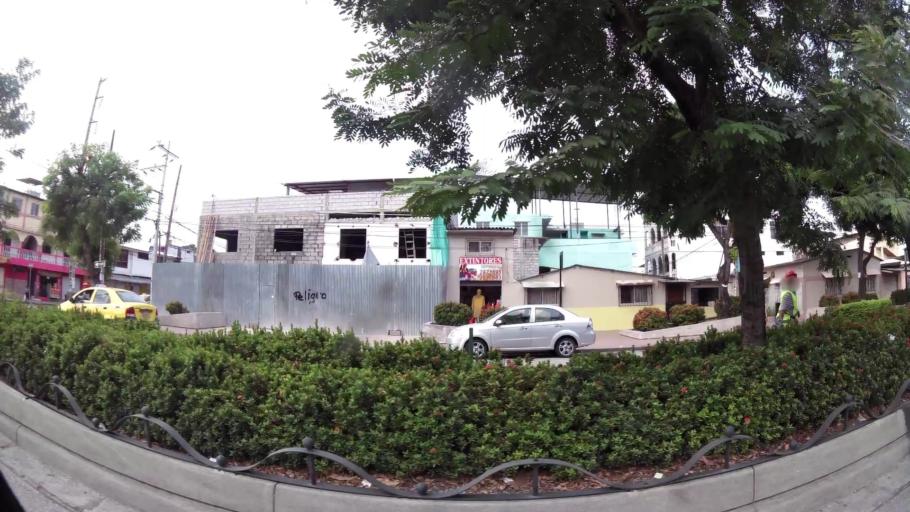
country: EC
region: Guayas
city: Eloy Alfaro
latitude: -2.1384
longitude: -79.8915
